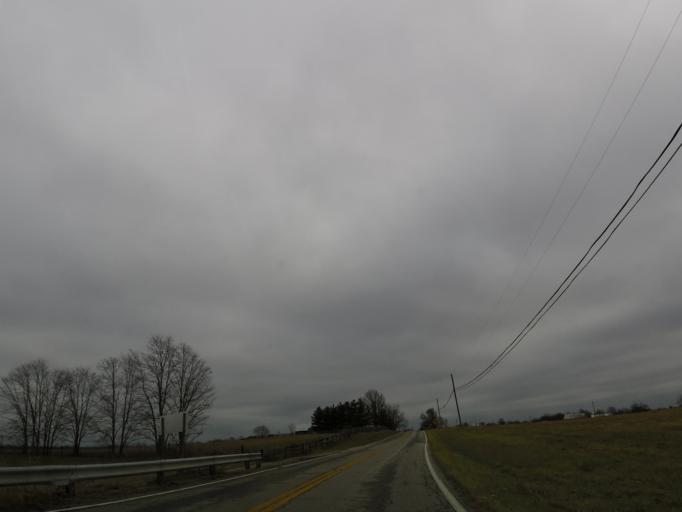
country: US
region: Kentucky
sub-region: Henry County
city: Eminence
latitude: 38.3492
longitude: -85.0642
